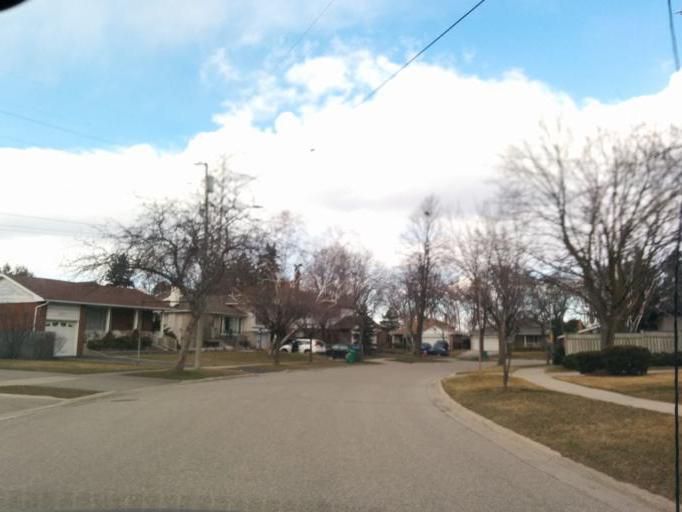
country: CA
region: Ontario
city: Etobicoke
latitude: 43.6075
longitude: -79.5684
